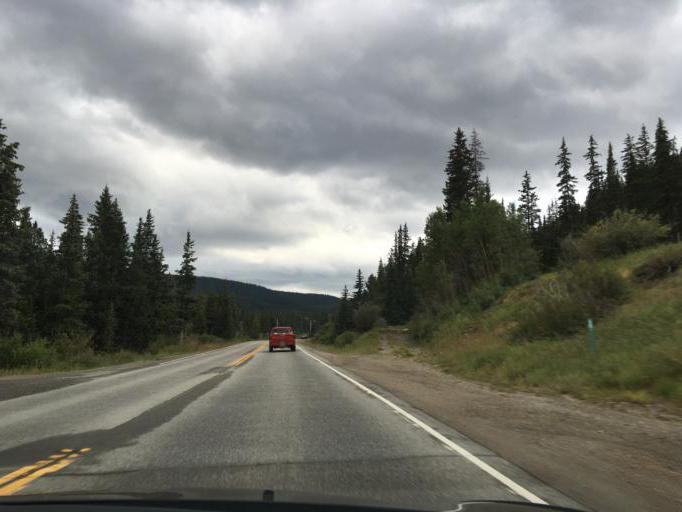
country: US
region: Colorado
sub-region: Summit County
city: Breckenridge
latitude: 39.3962
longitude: -106.0520
